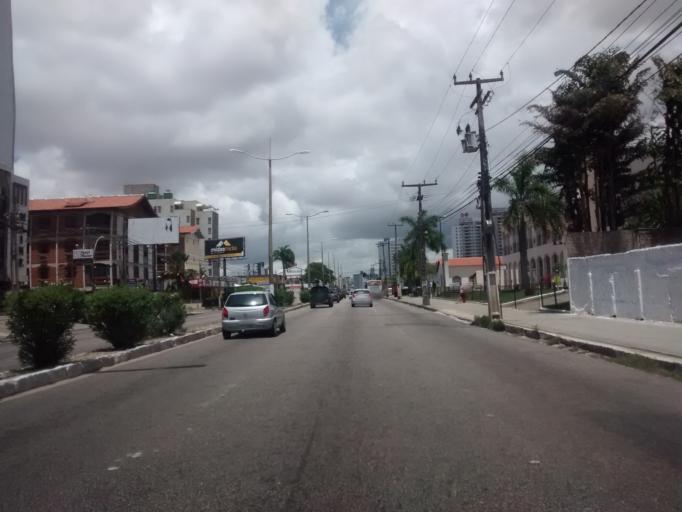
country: BR
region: Rio Grande do Norte
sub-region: Natal
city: Natal
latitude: -5.8195
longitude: -35.2076
